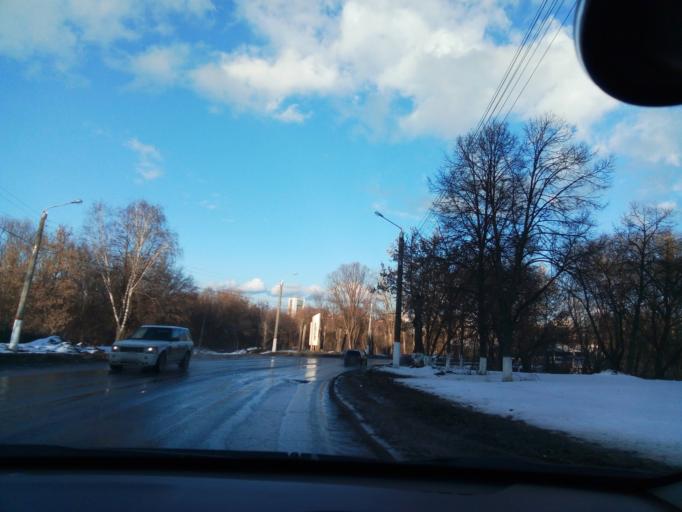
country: RU
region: Chuvashia
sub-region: Cheboksarskiy Rayon
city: Cheboksary
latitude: 56.1348
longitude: 47.2246
